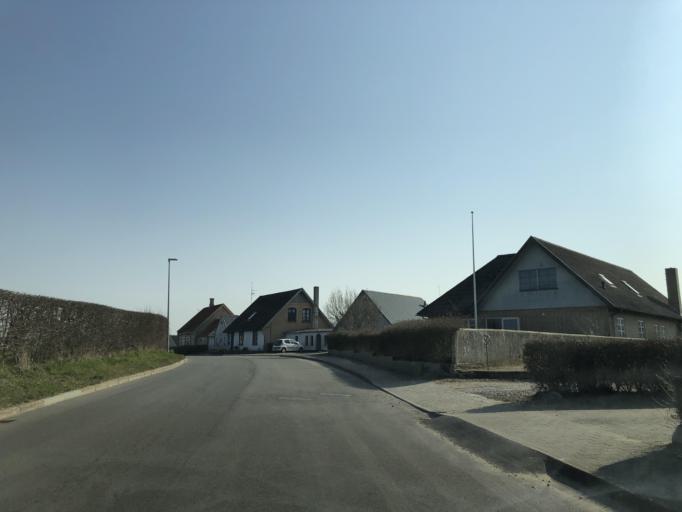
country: DK
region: South Denmark
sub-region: Sonderborg Kommune
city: Nordborg
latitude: 55.0619
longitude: 9.7394
